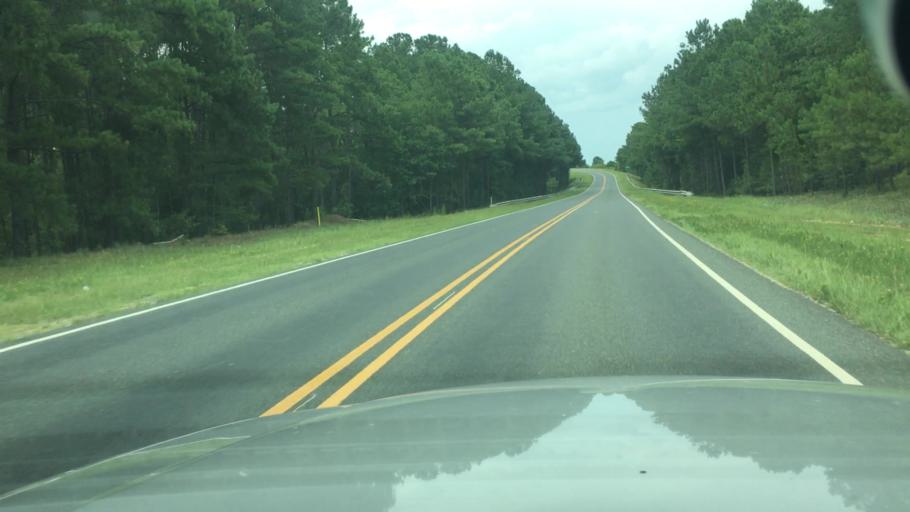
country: US
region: North Carolina
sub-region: Cumberland County
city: Hope Mills
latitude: 34.9784
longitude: -78.8928
